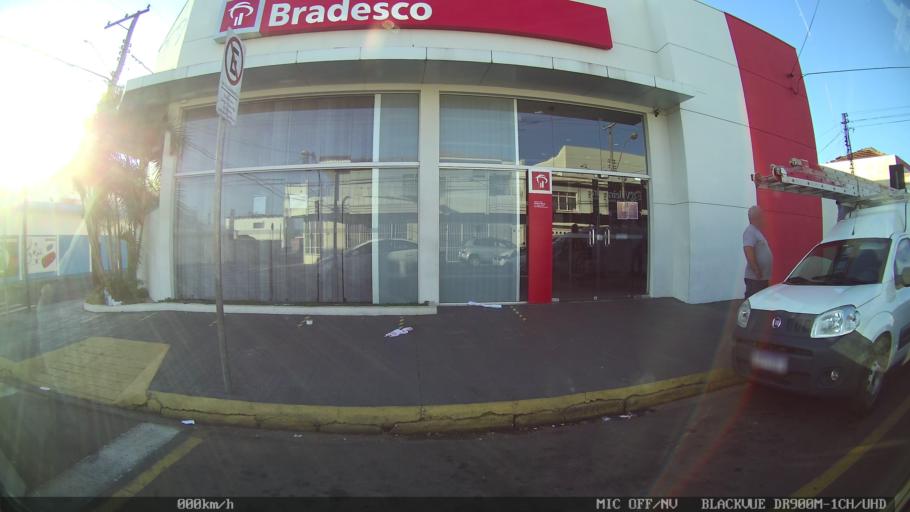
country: BR
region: Sao Paulo
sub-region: Franca
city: Franca
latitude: -20.5259
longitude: -47.3723
